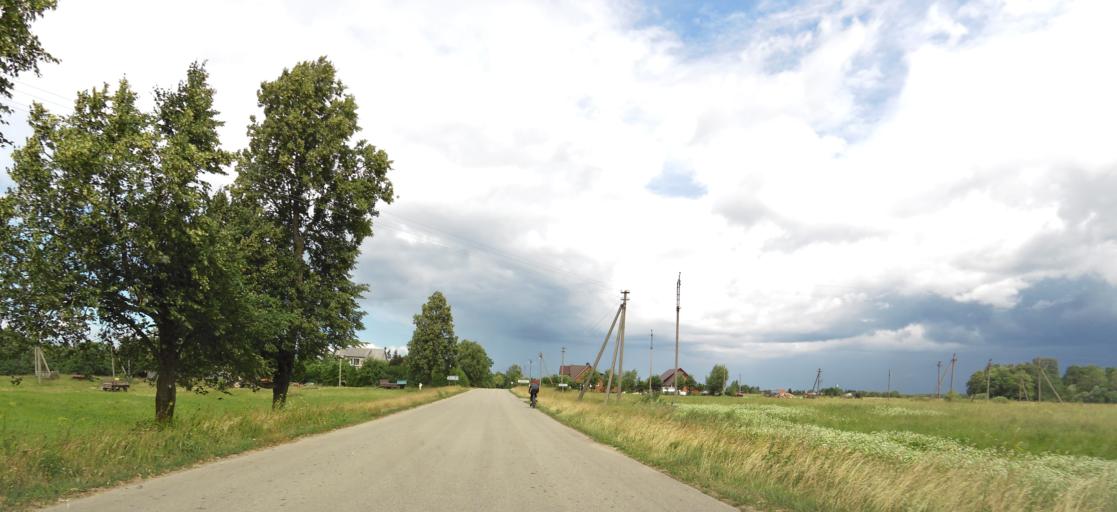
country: LT
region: Panevezys
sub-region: Birzai
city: Birzai
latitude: 56.3876
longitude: 24.7713
